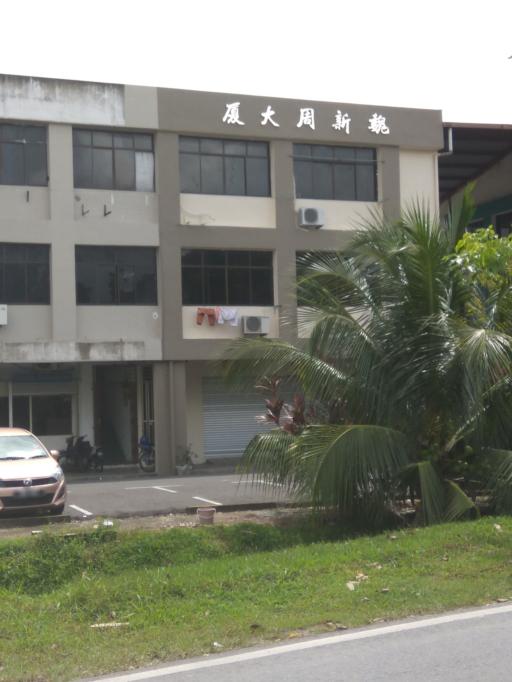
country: MY
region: Sarawak
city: Sibu
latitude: 2.2794
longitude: 111.8529
